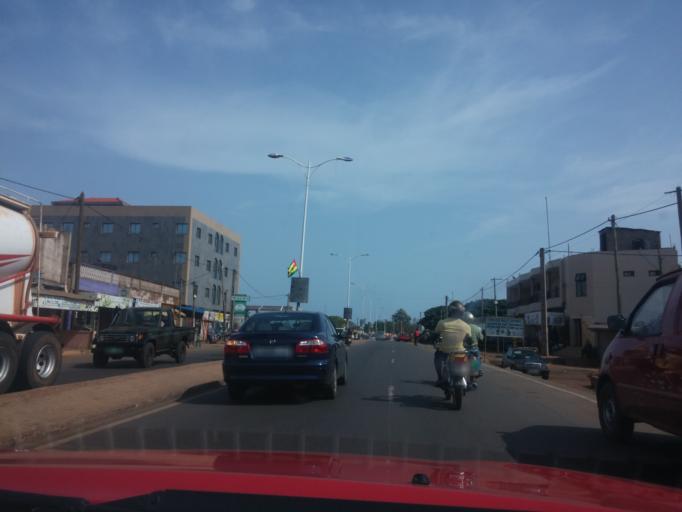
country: TG
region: Maritime
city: Lome
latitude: 6.2296
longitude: 1.2109
